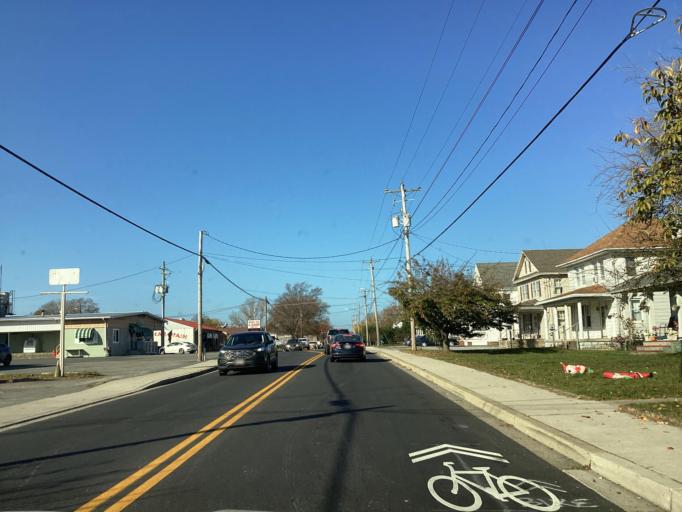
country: US
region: Maryland
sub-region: Dorchester County
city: Cambridge
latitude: 38.5613
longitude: -76.0712
